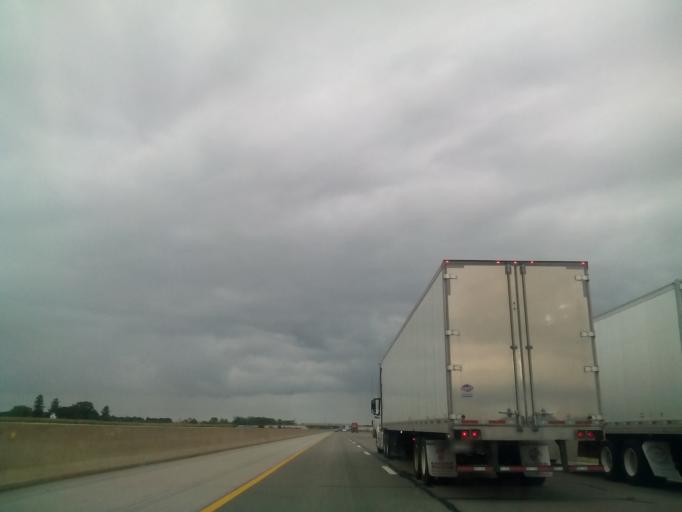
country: US
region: Ohio
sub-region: Sandusky County
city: Fremont
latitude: 41.3906
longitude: -83.0642
